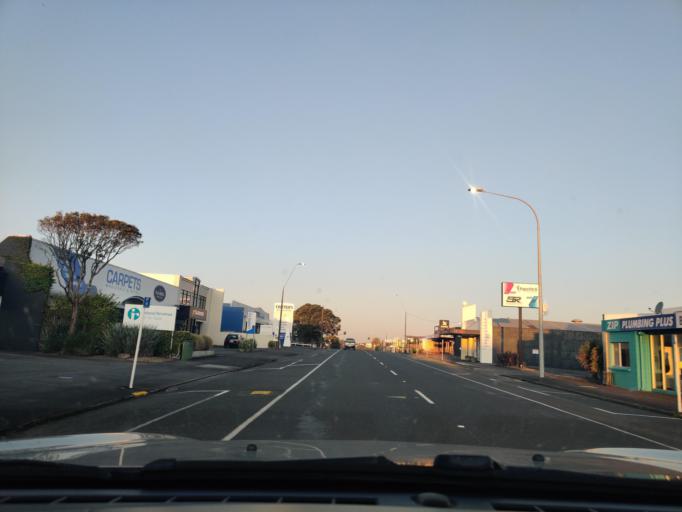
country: NZ
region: Taranaki
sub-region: New Plymouth District
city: New Plymouth
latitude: -39.0546
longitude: 174.0845
